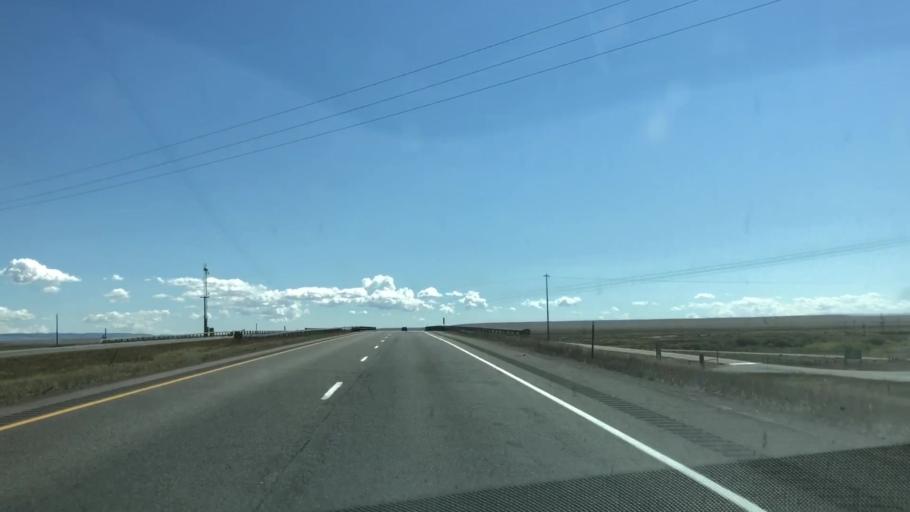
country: US
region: Wyoming
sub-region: Albany County
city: Laramie
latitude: 41.3963
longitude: -105.8254
